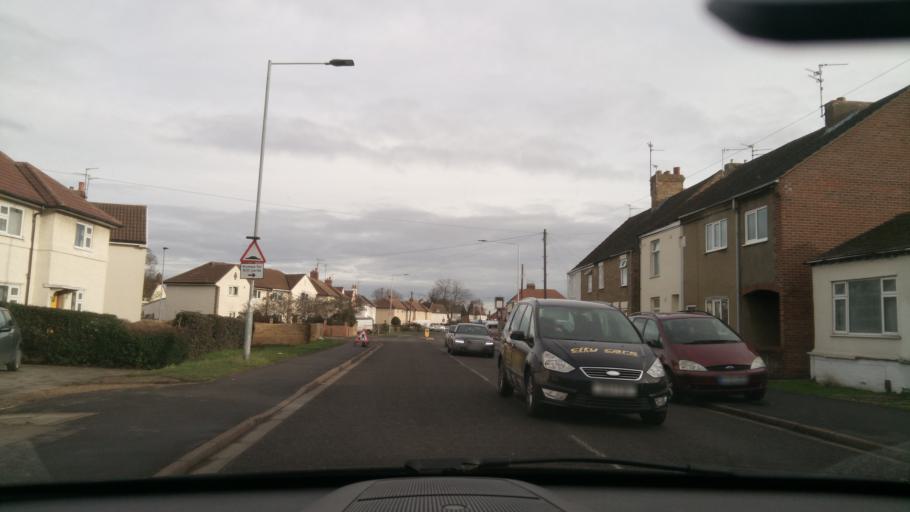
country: GB
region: England
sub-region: Peterborough
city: Peterborough
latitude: 52.5950
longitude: -0.2488
